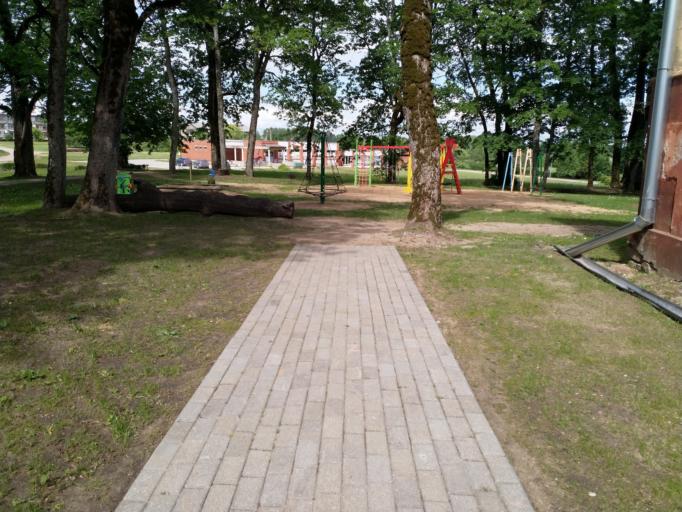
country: LV
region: Kuldigas Rajons
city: Kuldiga
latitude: 56.8404
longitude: 21.9452
